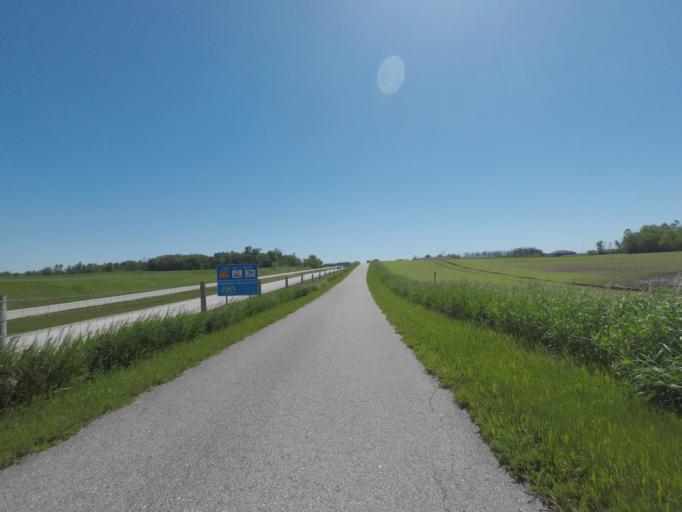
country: US
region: Wisconsin
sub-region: Sheboygan County
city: Sheboygan Falls
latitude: 43.7509
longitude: -87.8356
